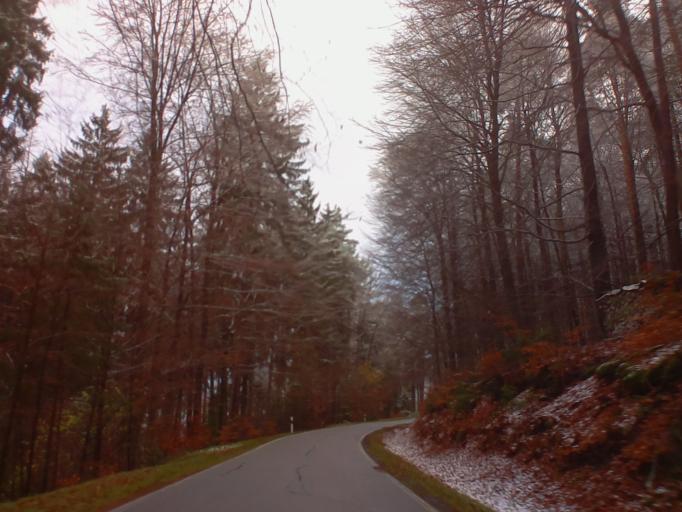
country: DE
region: Hesse
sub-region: Regierungsbezirk Darmstadt
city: Wald-Michelbach
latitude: 49.5449
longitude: 8.8728
